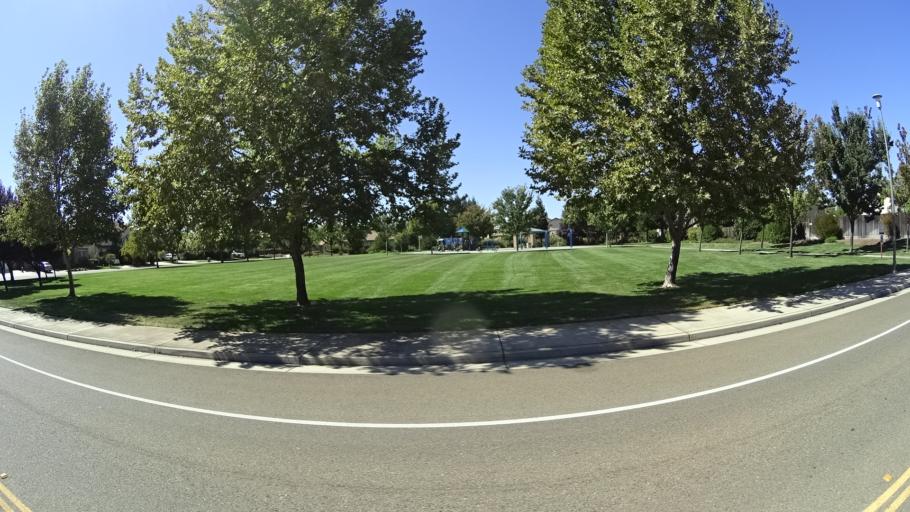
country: US
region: California
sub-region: Sacramento County
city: Elk Grove
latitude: 38.4063
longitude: -121.3387
